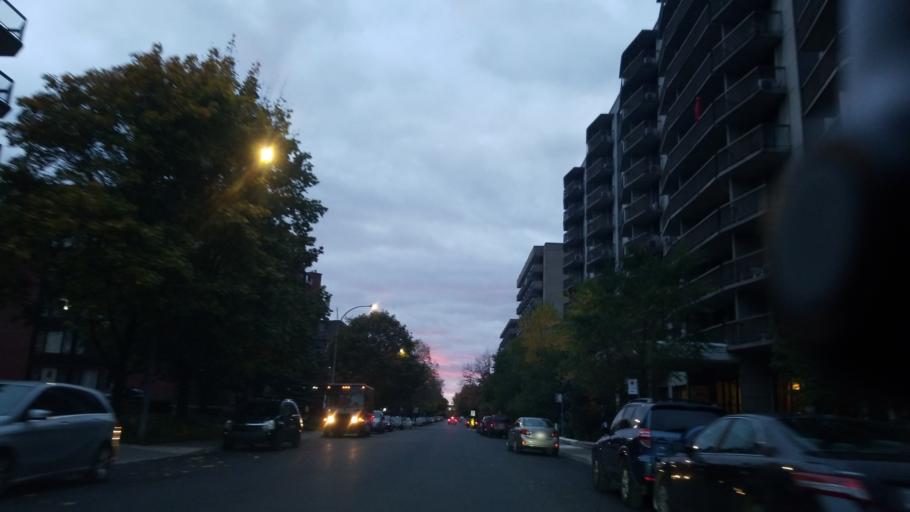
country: CA
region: Quebec
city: Mont-Royal
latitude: 45.5365
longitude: -73.6692
